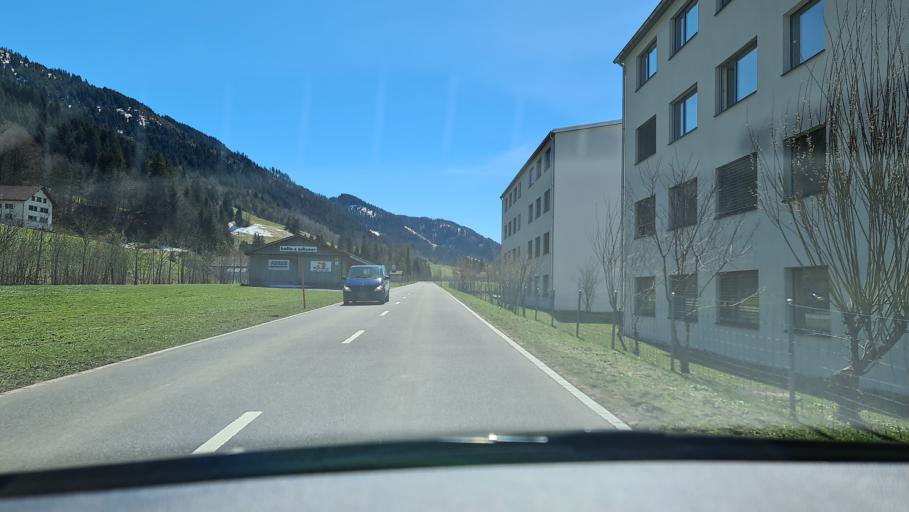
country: CH
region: Schwyz
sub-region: Bezirk Einsiedeln
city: Einsiedeln
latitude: 47.1002
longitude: 8.7280
